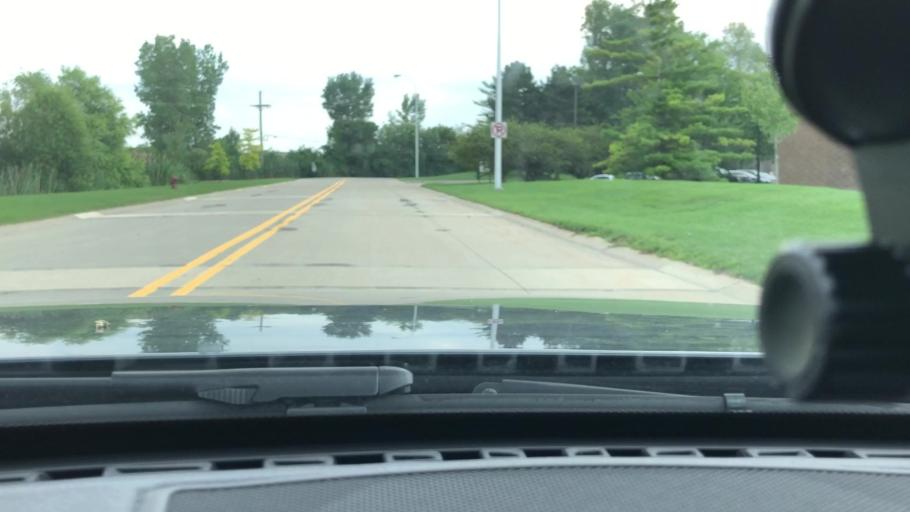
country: US
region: Michigan
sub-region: Wayne County
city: Livonia
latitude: 42.3744
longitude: -83.3397
